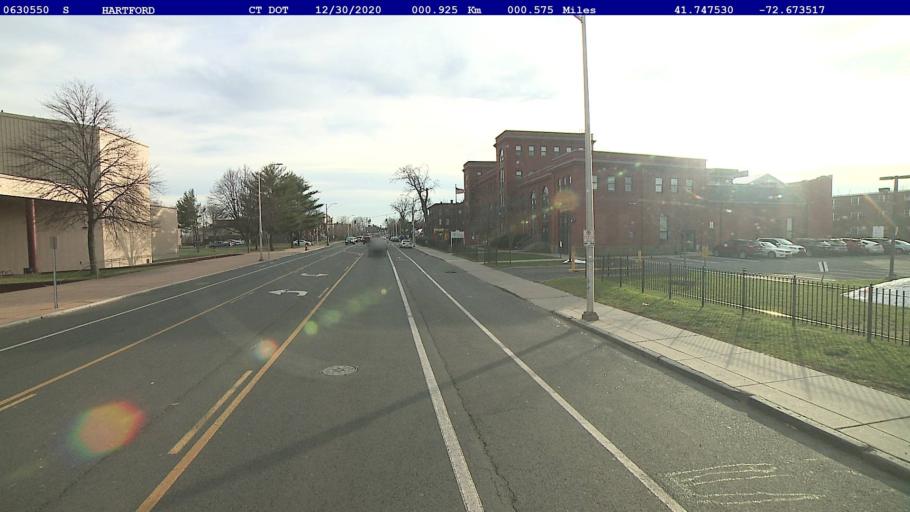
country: US
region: Connecticut
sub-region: Hartford County
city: Hartford
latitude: 41.7475
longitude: -72.6735
